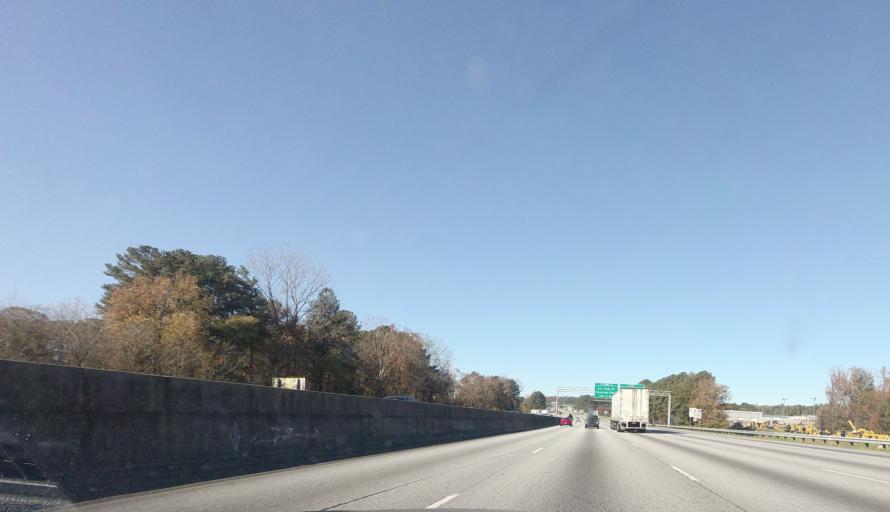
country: US
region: Georgia
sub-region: Cobb County
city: Mableton
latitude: 33.7716
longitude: -84.5455
